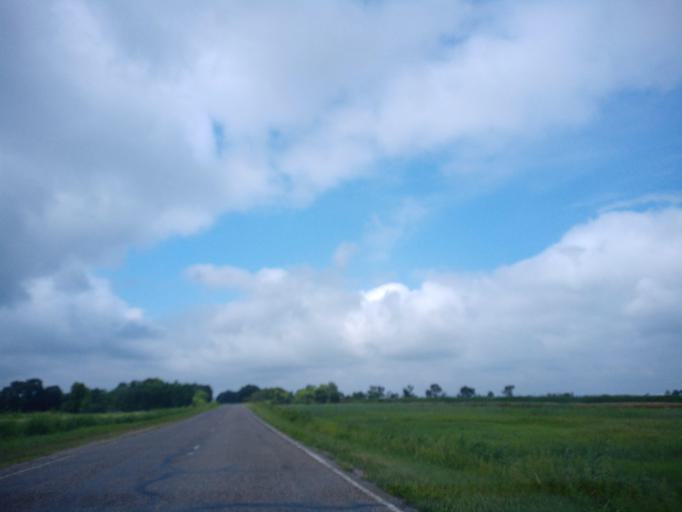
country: RU
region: Primorskiy
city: Dal'nerechensk
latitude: 45.9362
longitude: 133.8542
